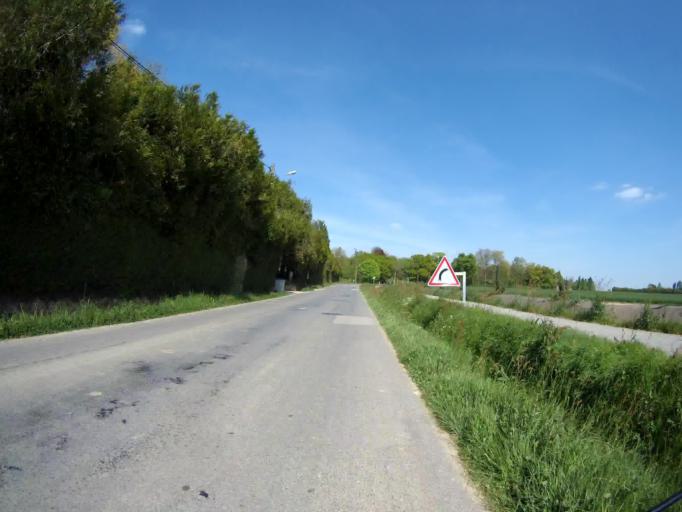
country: FR
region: Brittany
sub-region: Departement d'Ille-et-Vilaine
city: Saint-Erblon
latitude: 48.0234
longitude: -1.6412
